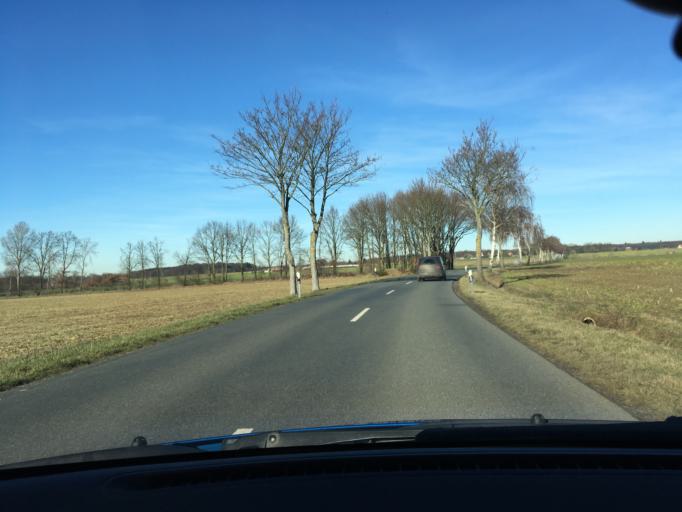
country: DE
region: Lower Saxony
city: Schwienau
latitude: 52.9925
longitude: 10.4422
